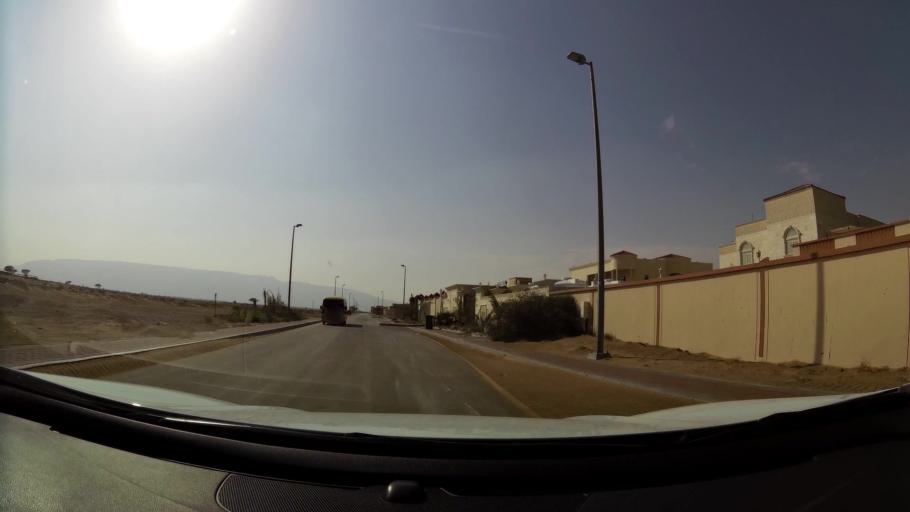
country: AE
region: Abu Dhabi
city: Al Ain
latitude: 24.0850
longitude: 55.9030
